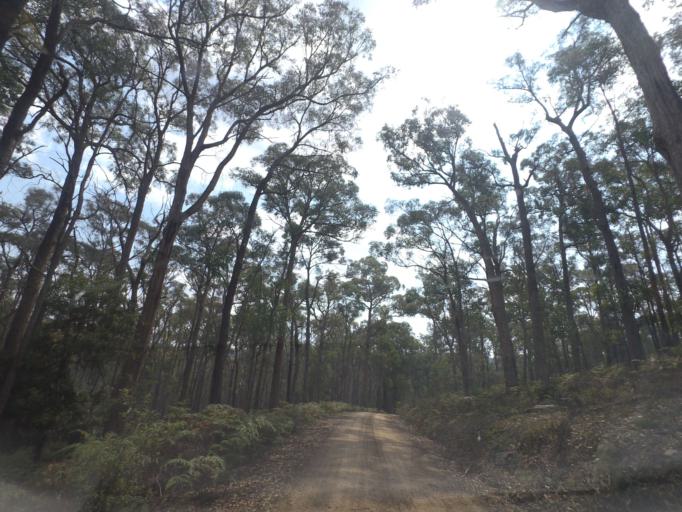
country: AU
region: Victoria
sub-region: Moorabool
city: Bacchus Marsh
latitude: -37.4644
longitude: 144.3680
